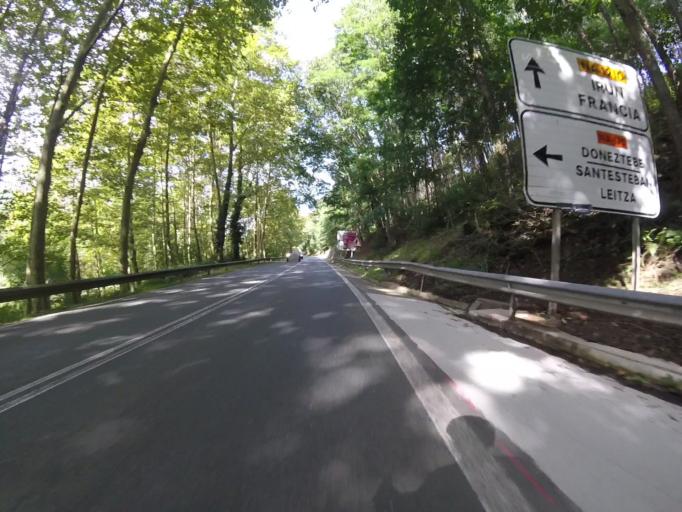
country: ES
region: Navarre
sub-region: Provincia de Navarra
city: Doneztebe
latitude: 43.1336
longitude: -1.6609
